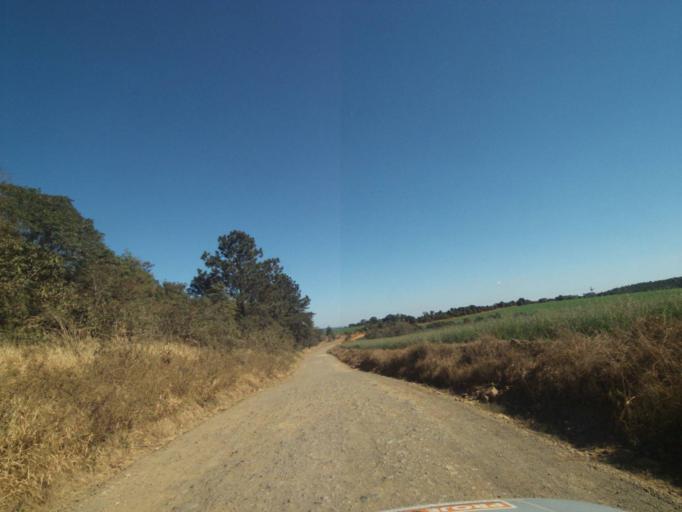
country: BR
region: Parana
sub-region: Reserva
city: Reserva
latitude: -24.6266
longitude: -50.6202
